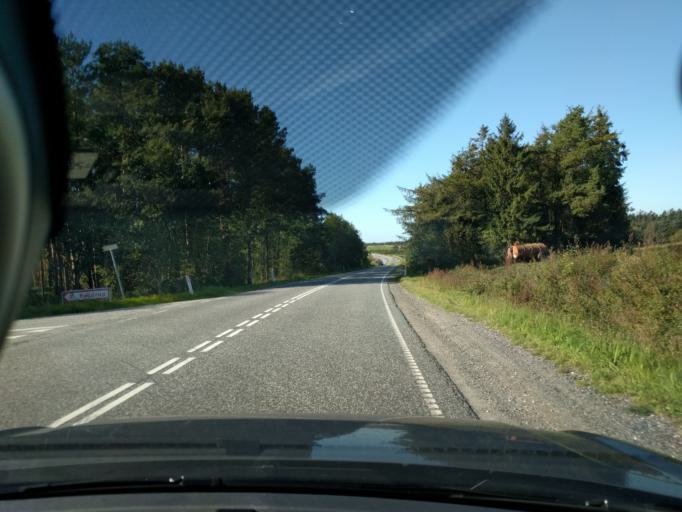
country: DK
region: North Denmark
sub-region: Mariagerfjord Kommune
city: Hobro
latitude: 56.6708
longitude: 9.7034
